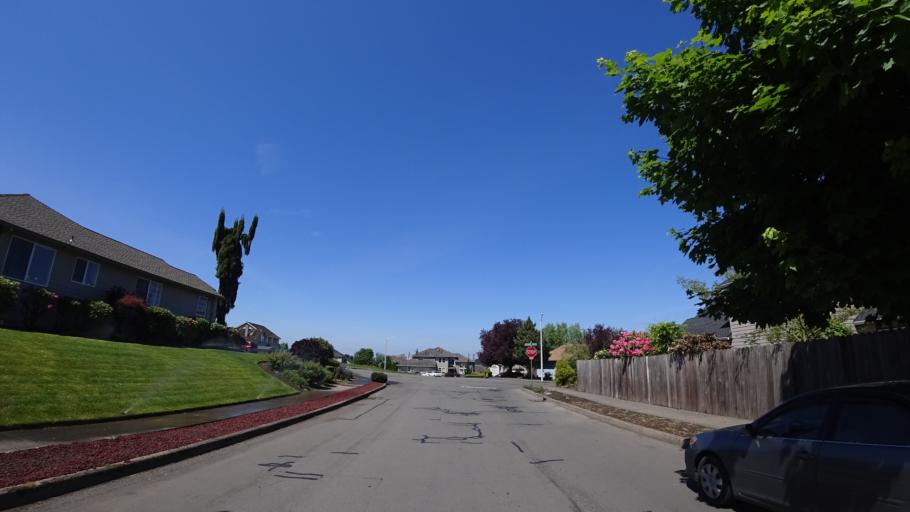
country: US
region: Oregon
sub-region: Multnomah County
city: Gresham
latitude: 45.4792
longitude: -122.4719
